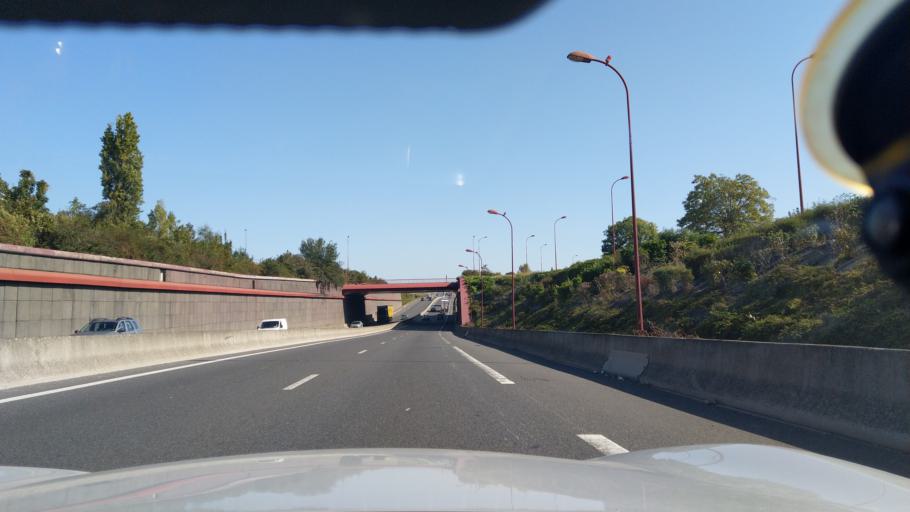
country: FR
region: Ile-de-France
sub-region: Departement du Val-d'Oise
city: Gonesse
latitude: 48.9821
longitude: 2.4681
